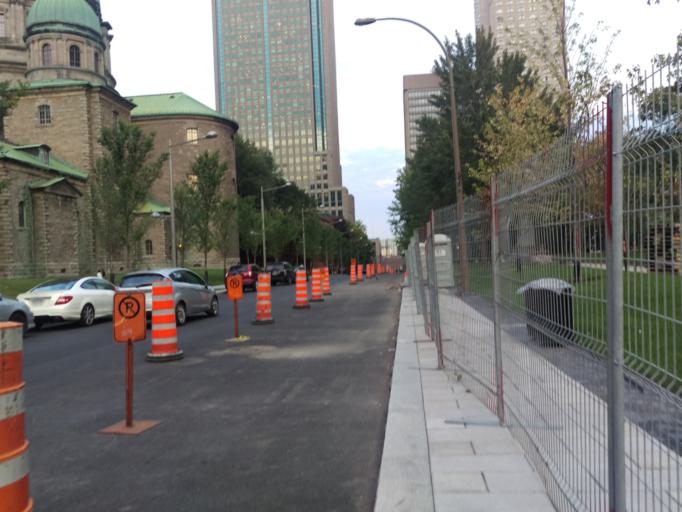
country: CA
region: Quebec
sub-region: Montreal
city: Montreal
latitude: 45.4991
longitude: -73.5697
